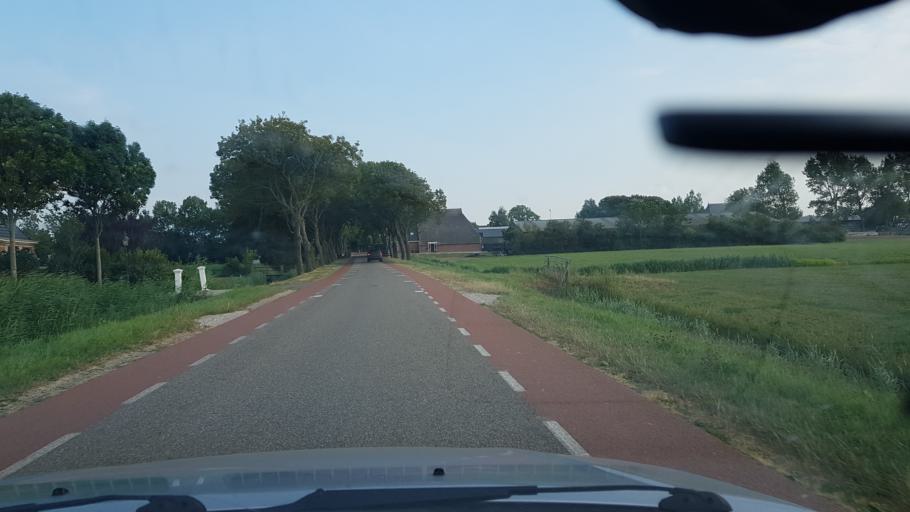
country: NL
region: Friesland
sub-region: Gemeente Ferwerderadiel
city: Burdaard
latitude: 53.3256
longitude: 5.8739
